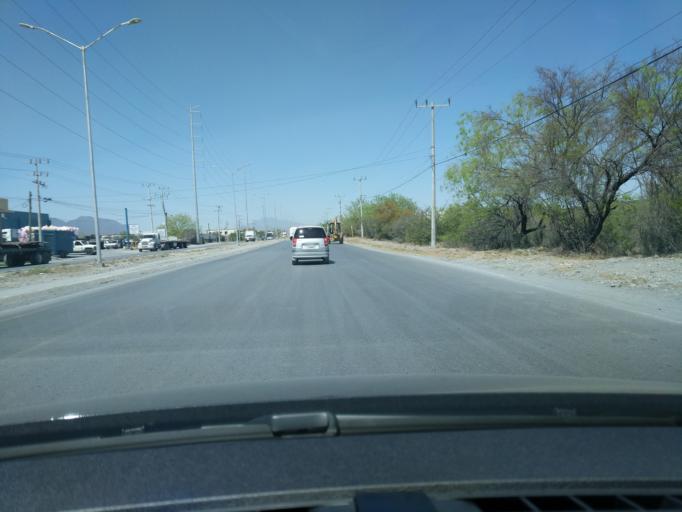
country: MX
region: Nuevo Leon
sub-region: Salinas Victoria
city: Emiliano Zapata
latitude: 25.9030
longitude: -100.2636
